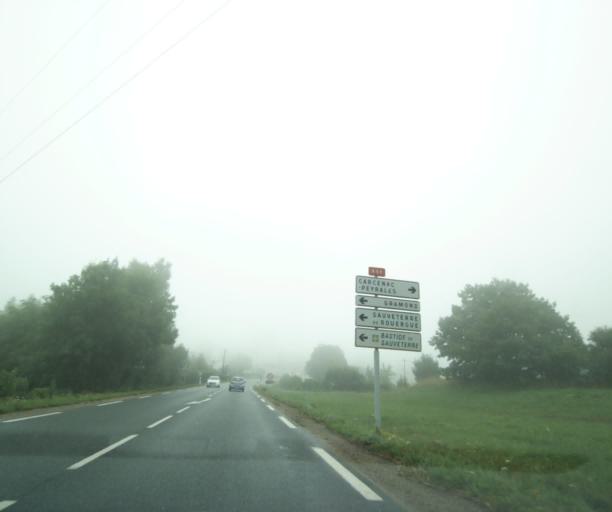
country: FR
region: Midi-Pyrenees
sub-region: Departement de l'Aveyron
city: Baraqueville
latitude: 44.2691
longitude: 2.4195
